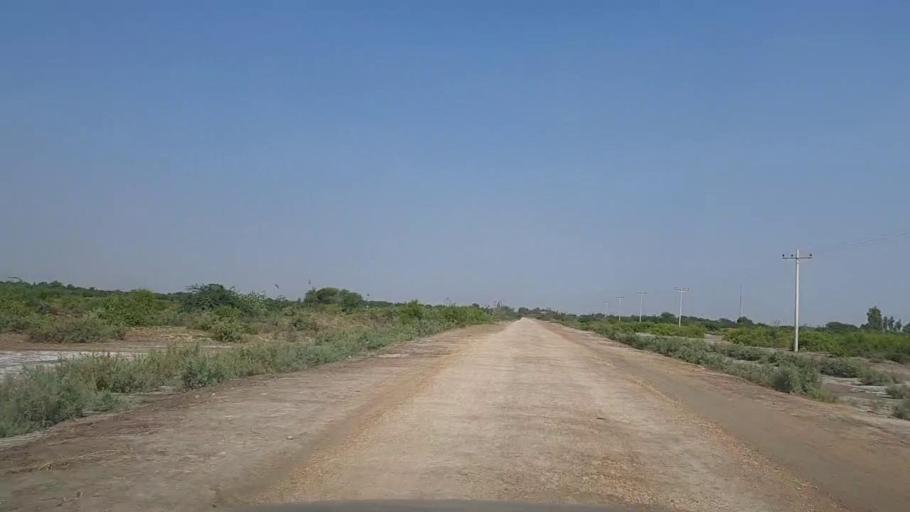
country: PK
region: Sindh
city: Thatta
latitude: 24.6082
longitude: 67.9556
